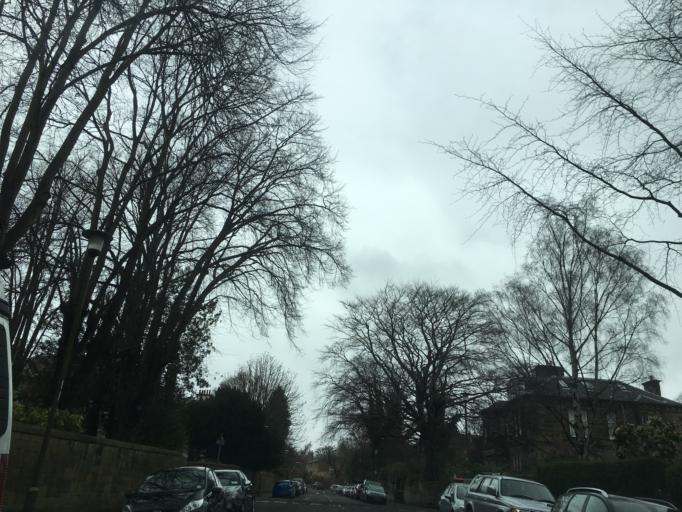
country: GB
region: Scotland
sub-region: Edinburgh
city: Edinburgh
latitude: 55.9311
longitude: -3.1820
